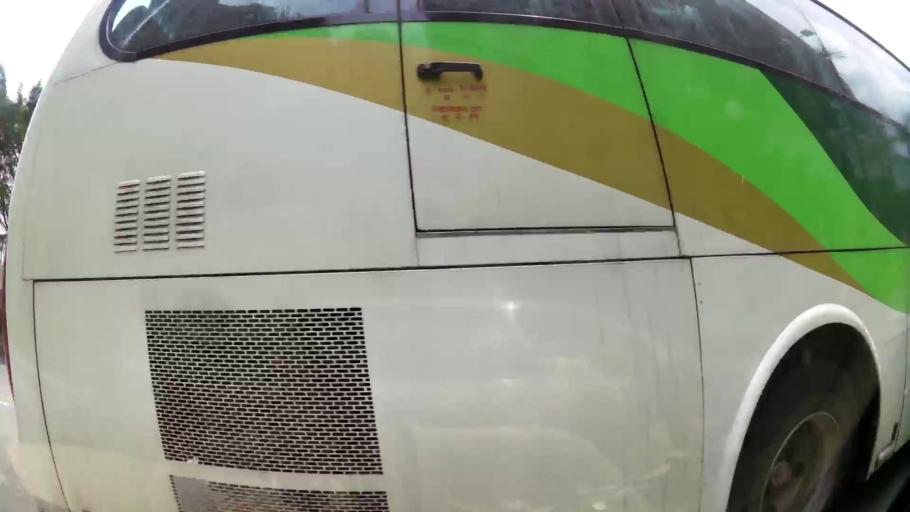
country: HK
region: Sham Shui Po
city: Sham Shui Po
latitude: 22.3328
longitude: 114.1495
